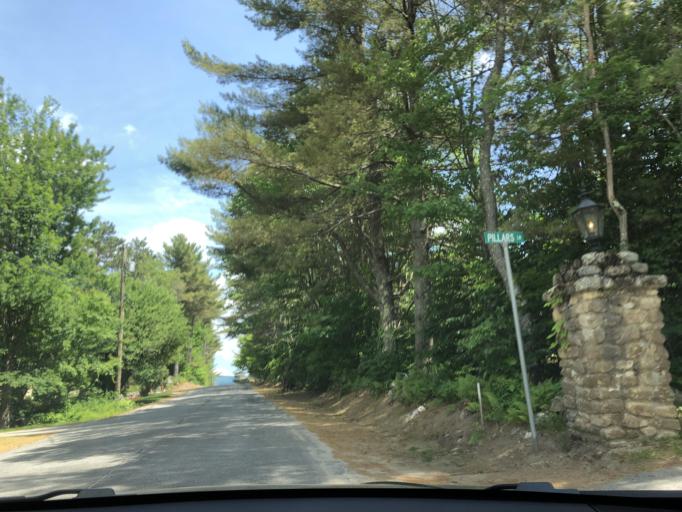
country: US
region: New Hampshire
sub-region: Merrimack County
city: New London
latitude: 43.4109
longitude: -72.0027
